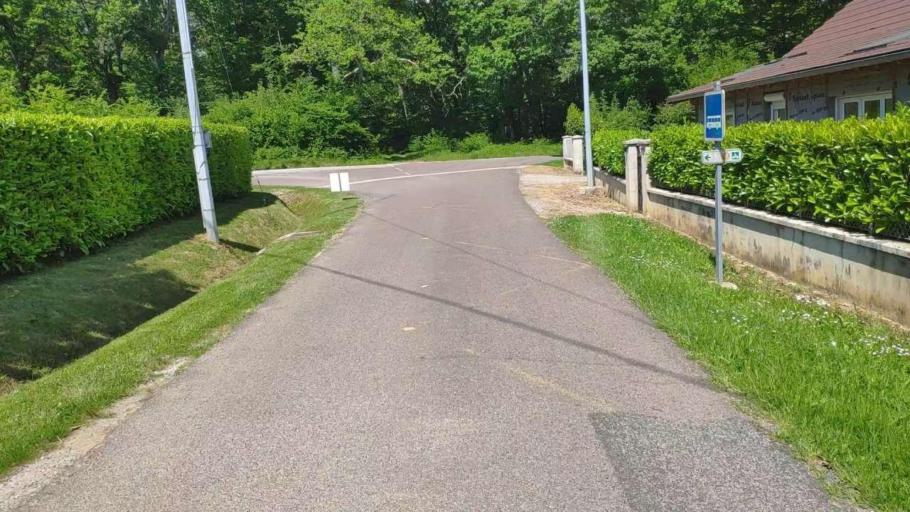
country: FR
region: Franche-Comte
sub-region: Departement du Jura
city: Bletterans
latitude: 46.8046
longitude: 5.4289
